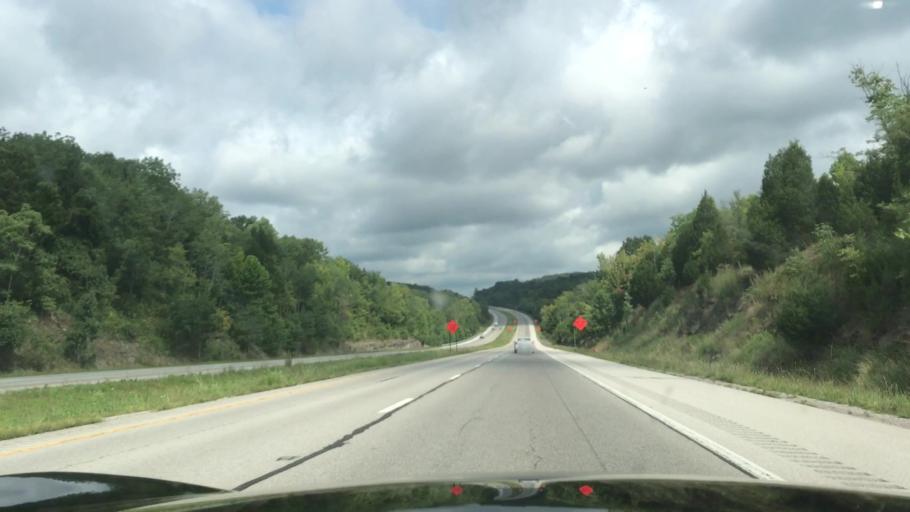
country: US
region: Kentucky
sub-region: Butler County
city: Morgantown
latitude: 37.0858
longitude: -86.6225
